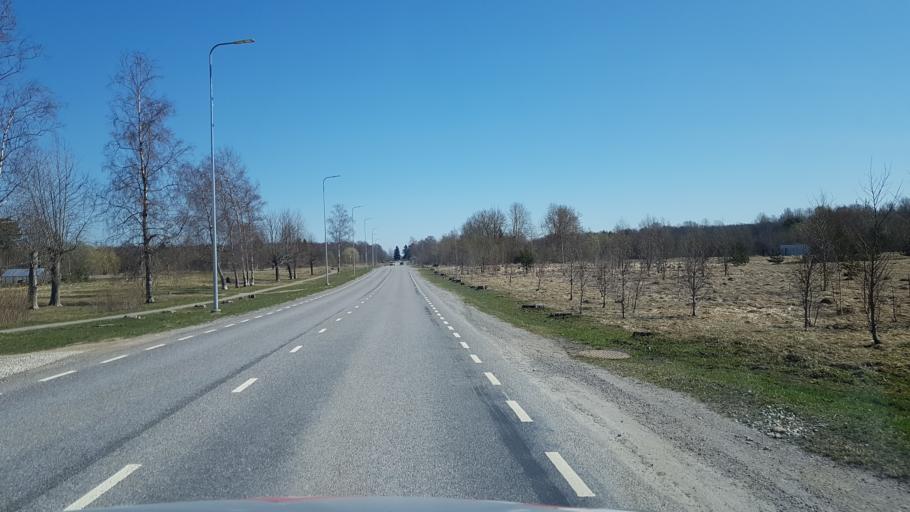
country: EE
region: Ida-Virumaa
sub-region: Kohtla-Jaerve linn
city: Kohtla-Jarve
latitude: 59.3372
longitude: 27.2944
